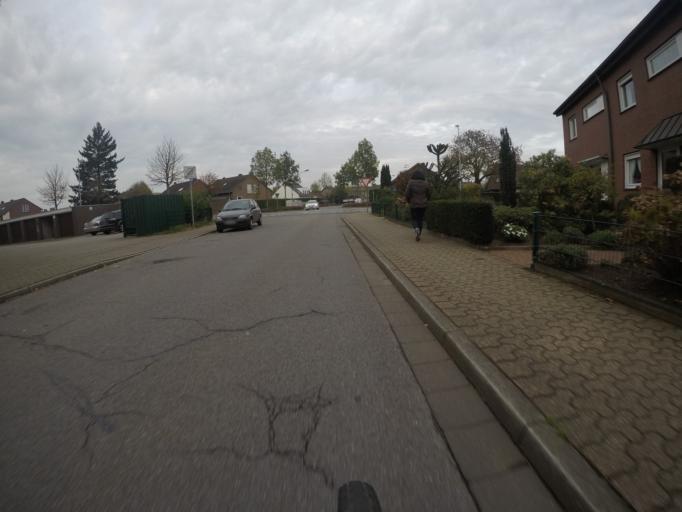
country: DE
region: North Rhine-Westphalia
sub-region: Regierungsbezirk Dusseldorf
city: Bocholt
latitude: 51.8240
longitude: 6.6231
